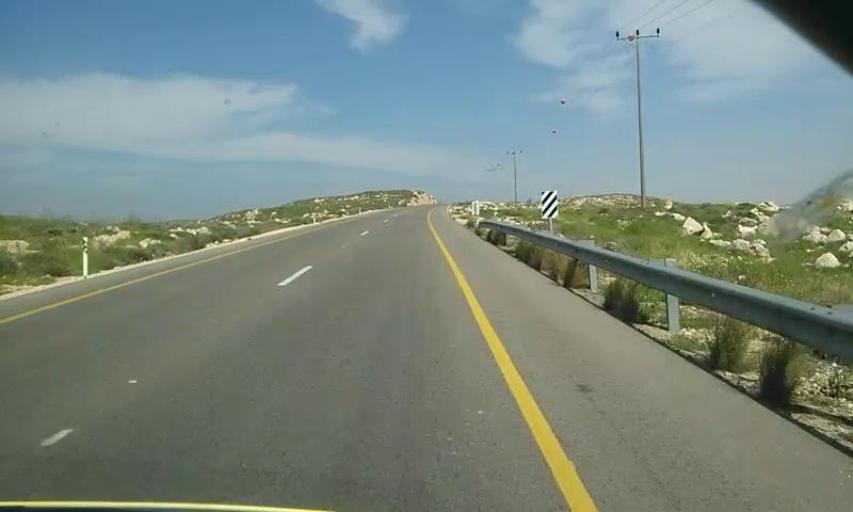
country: PS
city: Rabud
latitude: 31.3931
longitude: 35.0177
